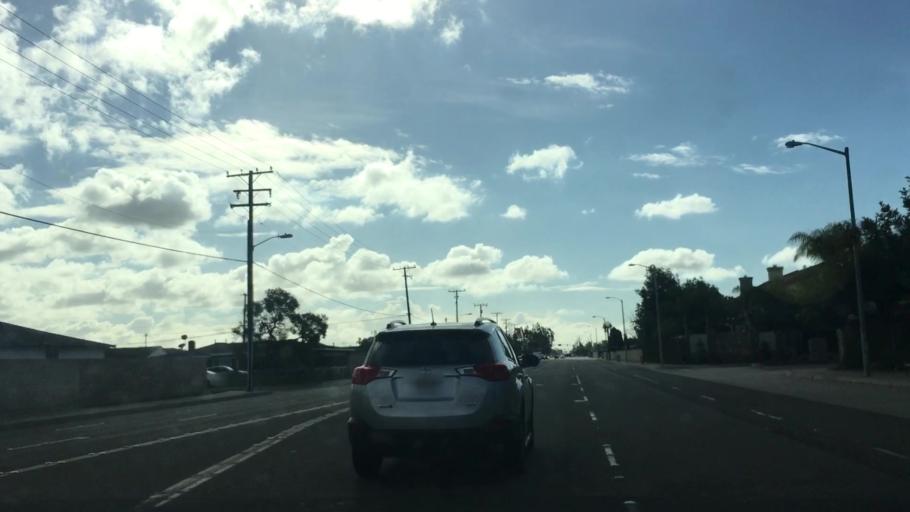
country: US
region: California
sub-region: Orange County
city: Midway City
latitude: 33.7496
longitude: -117.9724
